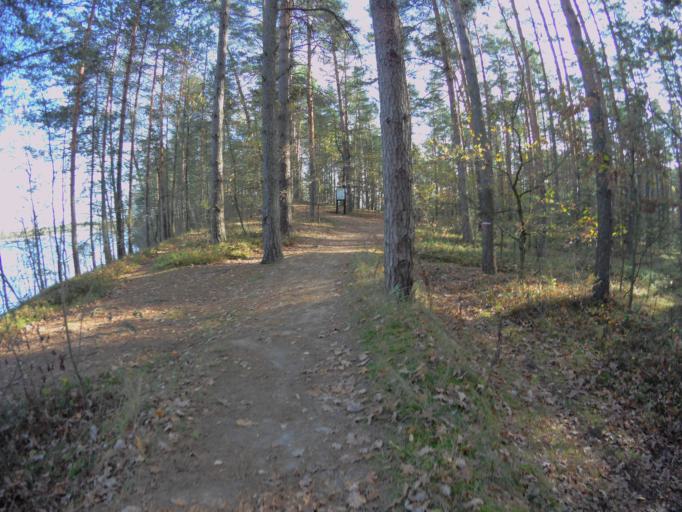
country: PL
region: Subcarpathian Voivodeship
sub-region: Powiat kolbuszowski
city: Lipnica
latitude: 50.3391
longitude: 21.9292
